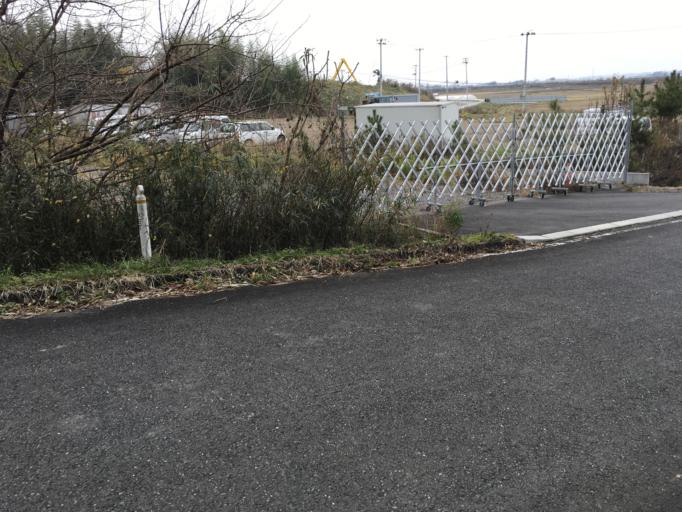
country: JP
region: Miyagi
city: Wakuya
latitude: 38.6826
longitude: 141.2754
